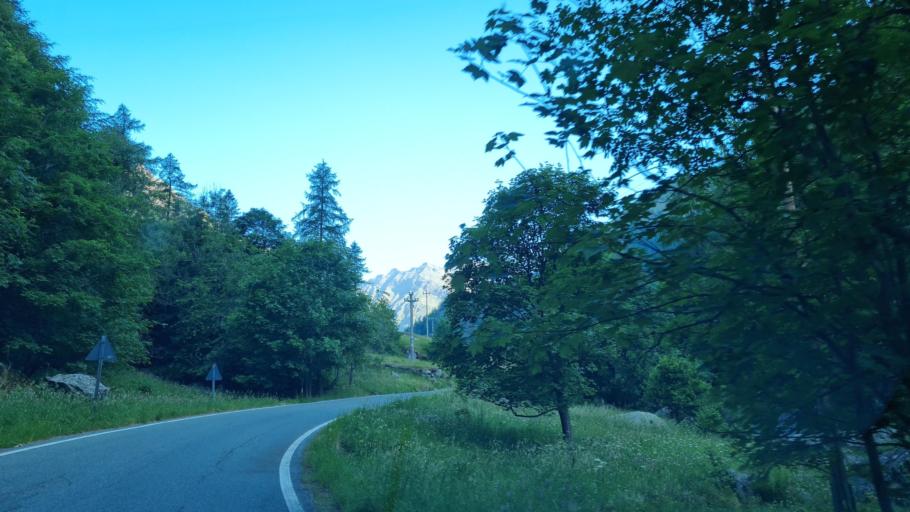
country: IT
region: Piedmont
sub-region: Provincia di Torino
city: Valprato Soana
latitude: 45.5381
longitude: 7.5370
